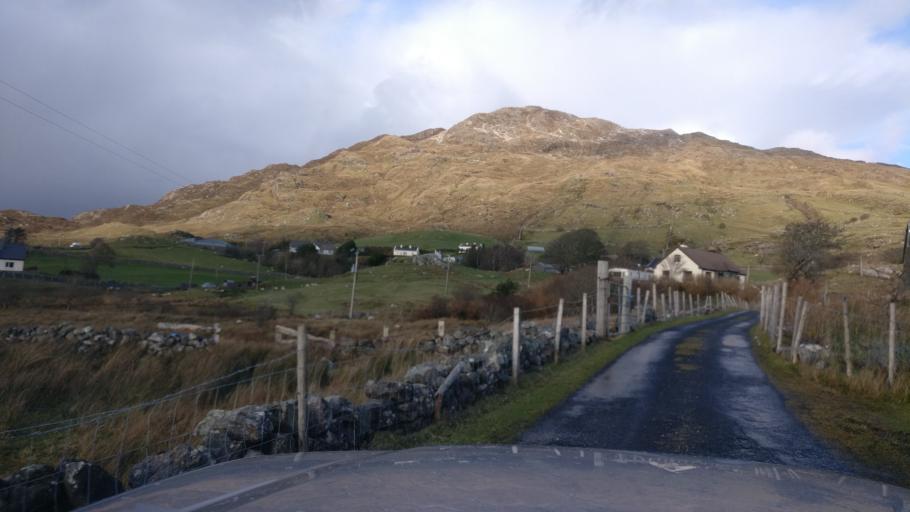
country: IE
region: Connaught
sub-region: County Galway
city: Clifden
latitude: 53.4744
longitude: -9.7281
